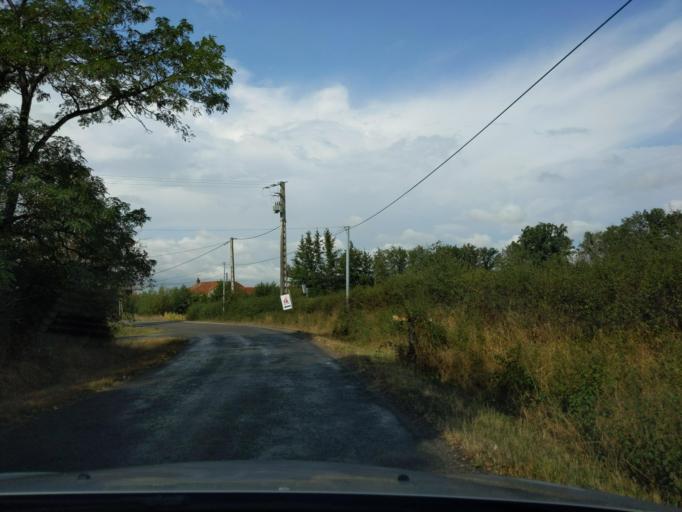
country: FR
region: Bourgogne
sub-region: Departement de Saone-et-Loire
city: Bourbon-Lancy
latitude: 46.6403
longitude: 3.7421
